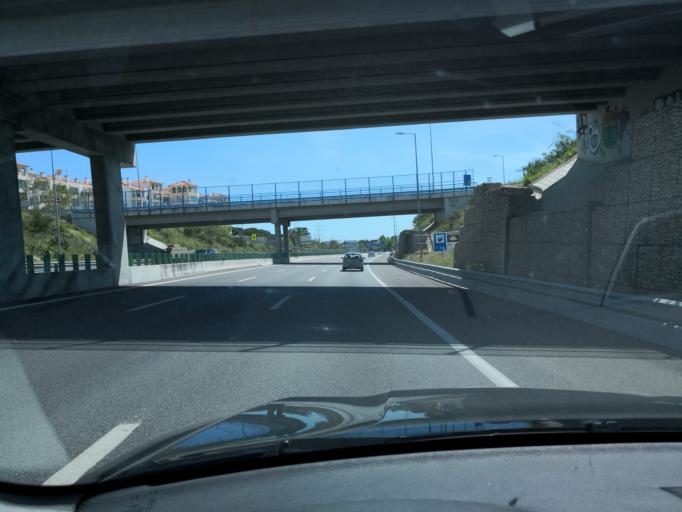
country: PT
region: Setubal
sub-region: Almada
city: Sobreda
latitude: 38.6481
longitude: -9.2009
